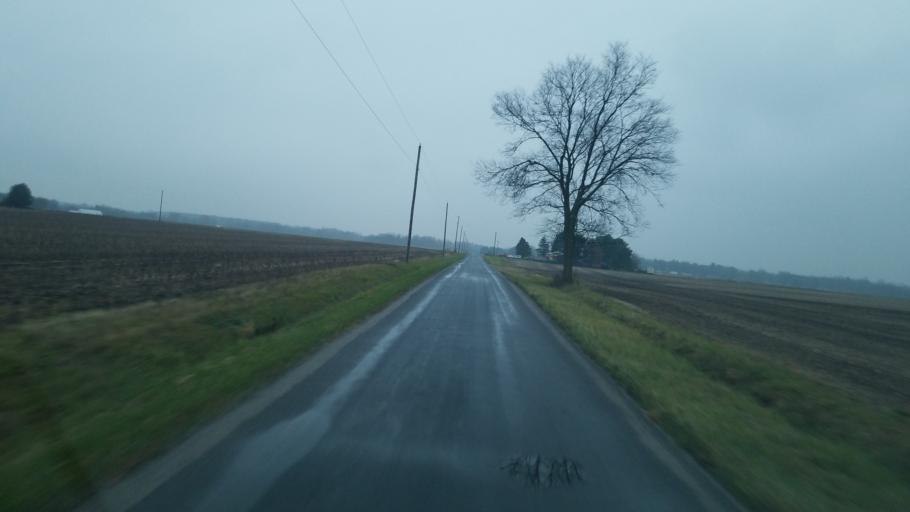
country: US
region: Ohio
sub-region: Delaware County
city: Ashley
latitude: 40.4425
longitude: -82.9904
